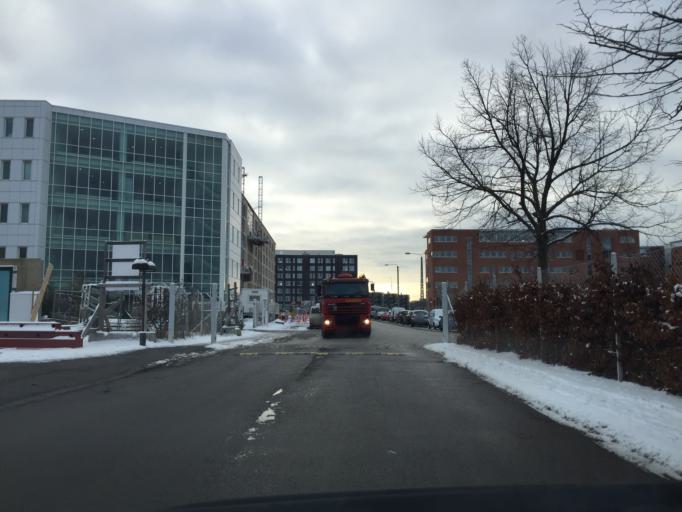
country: DK
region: Capital Region
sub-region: Kobenhavn
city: Copenhagen
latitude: 55.6544
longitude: 12.5482
